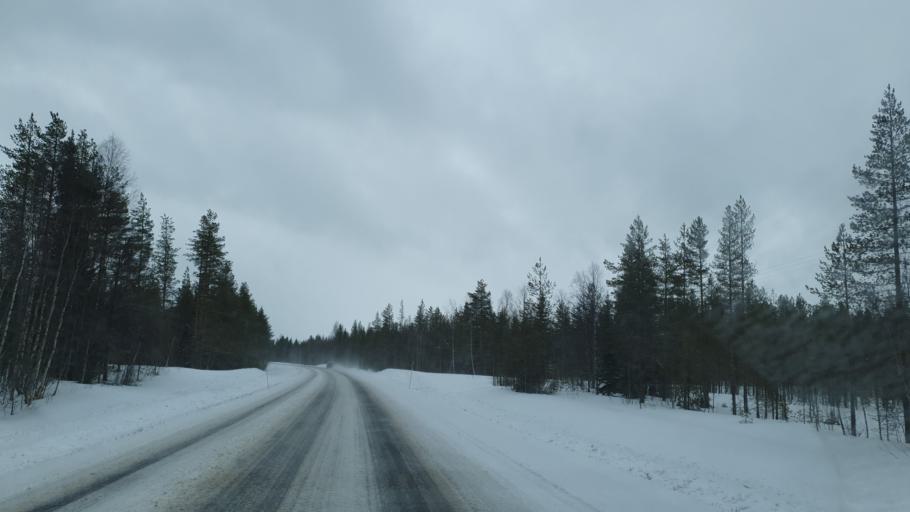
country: FI
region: Lapland
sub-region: Rovaniemi
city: Ranua
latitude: 66.1340
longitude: 26.2781
